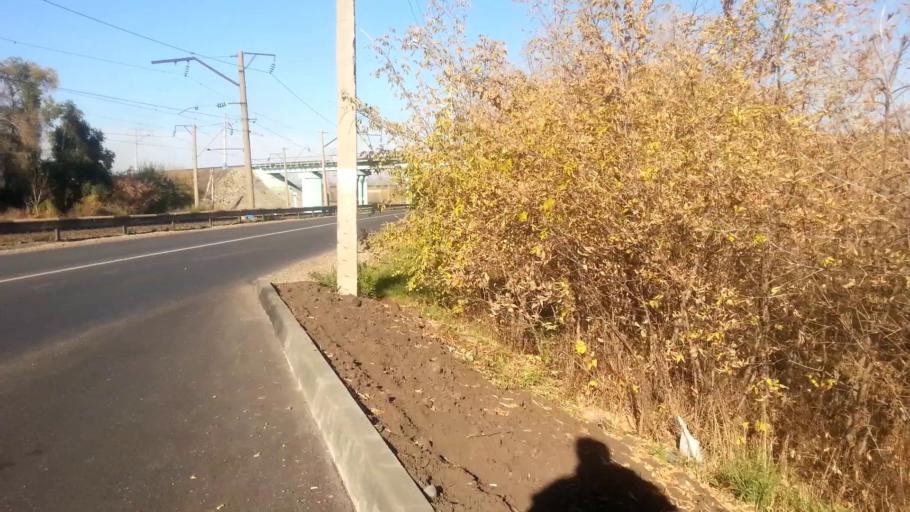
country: RU
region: Altai Krai
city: Novoaltaysk
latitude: 53.3757
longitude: 83.9356
